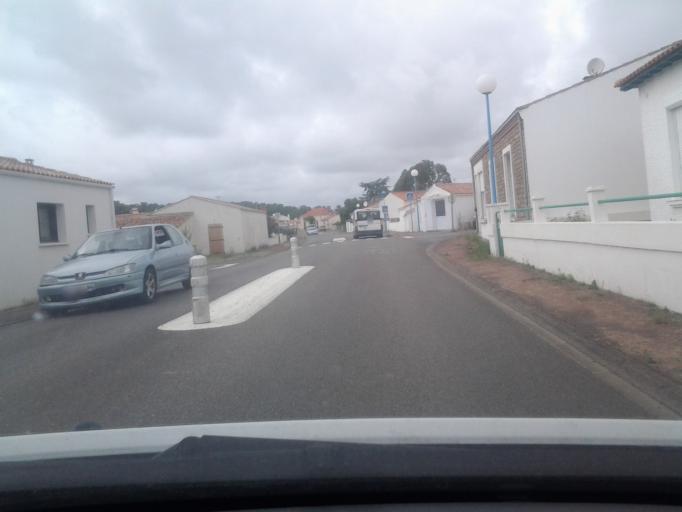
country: FR
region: Pays de la Loire
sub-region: Departement de la Vendee
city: Longeville-sur-Mer
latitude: 46.3862
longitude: -1.4681
